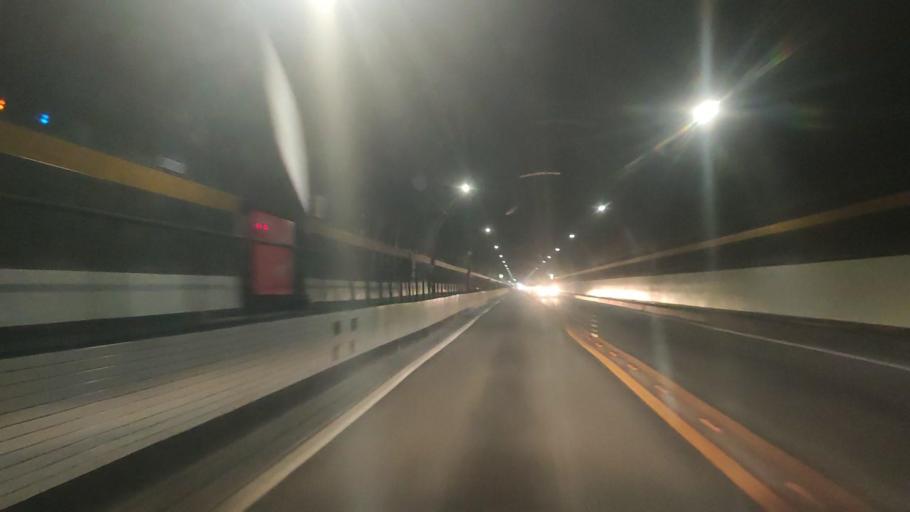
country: JP
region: Nagasaki
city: Obita
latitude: 32.7801
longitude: 129.8861
